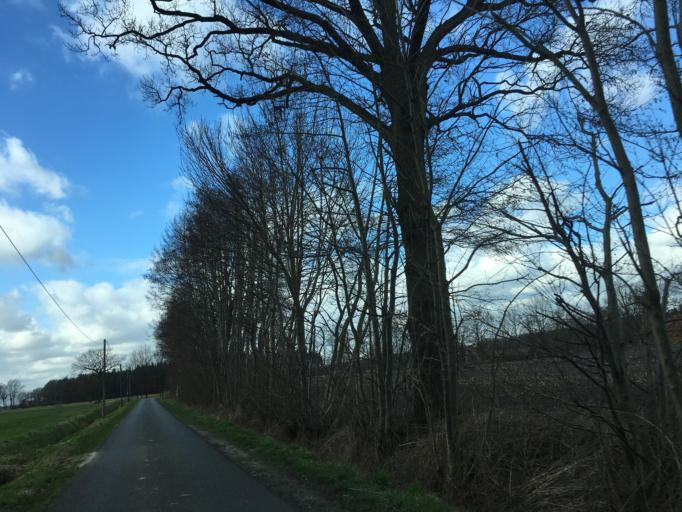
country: DE
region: North Rhine-Westphalia
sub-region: Regierungsbezirk Munster
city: Steinfurt
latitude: 52.1192
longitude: 7.3237
